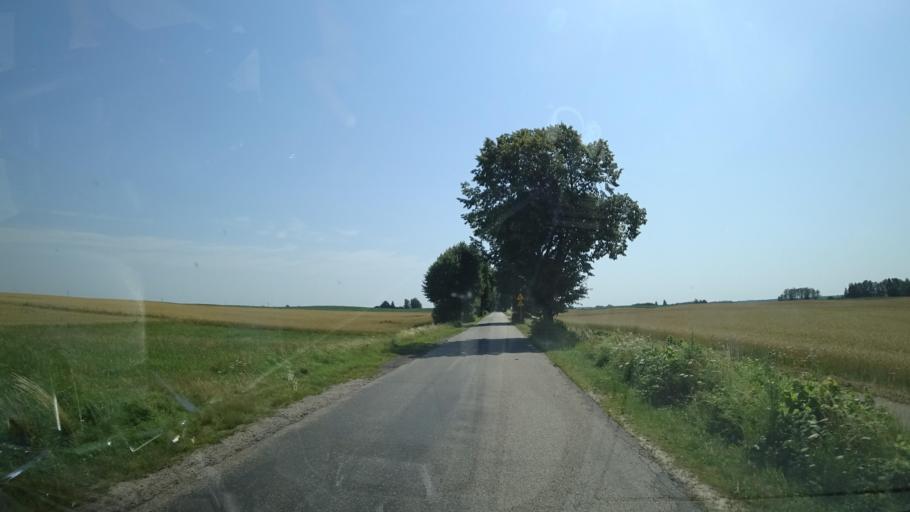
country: PL
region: Pomeranian Voivodeship
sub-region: Powiat chojnicki
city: Brusy
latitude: 53.8791
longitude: 17.6494
